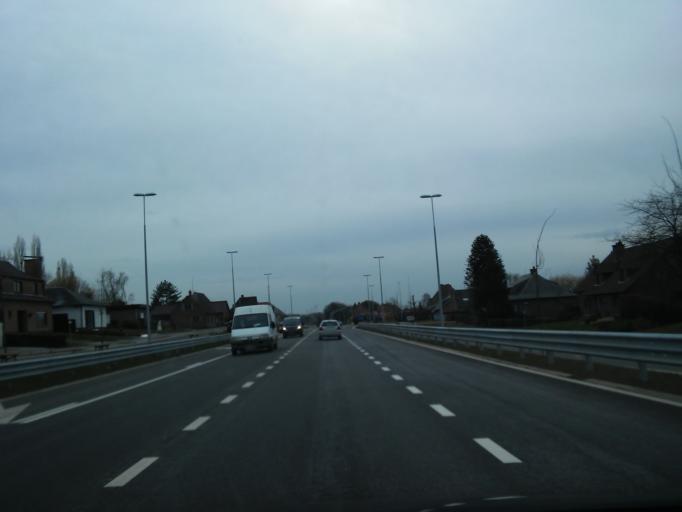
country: BE
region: Flanders
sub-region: Provincie Oost-Vlaanderen
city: Hamme
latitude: 51.1182
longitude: 4.1437
